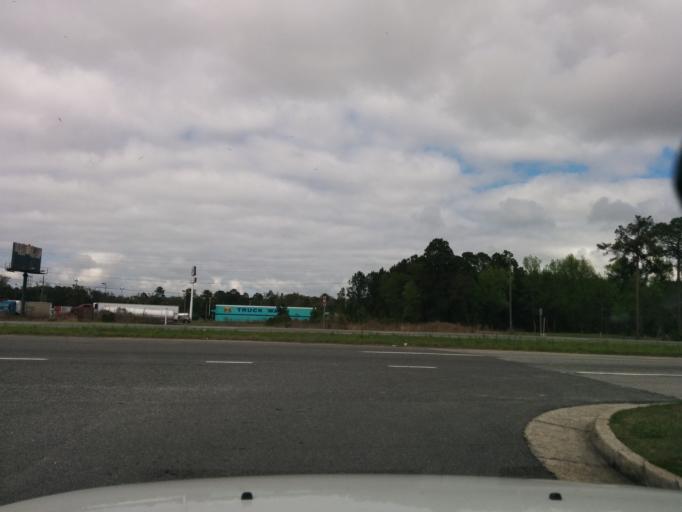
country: US
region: Georgia
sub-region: Glynn County
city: Brunswick
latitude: 31.1358
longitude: -81.5709
